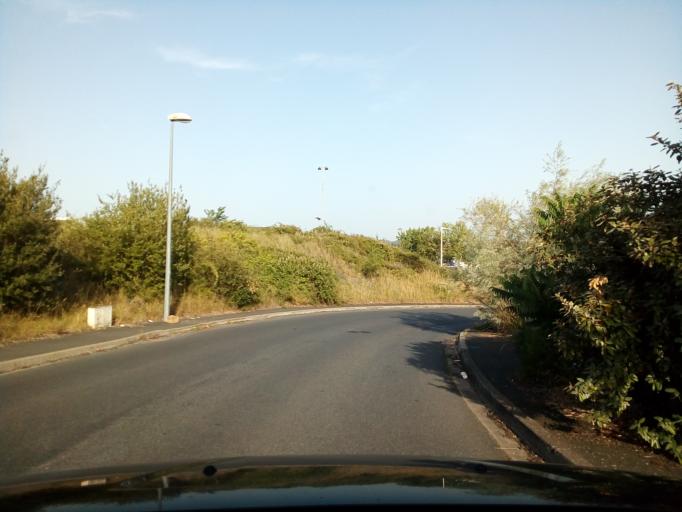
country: FR
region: Auvergne
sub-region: Departement de l'Allier
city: Montlucon
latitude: 46.3389
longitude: 2.5660
